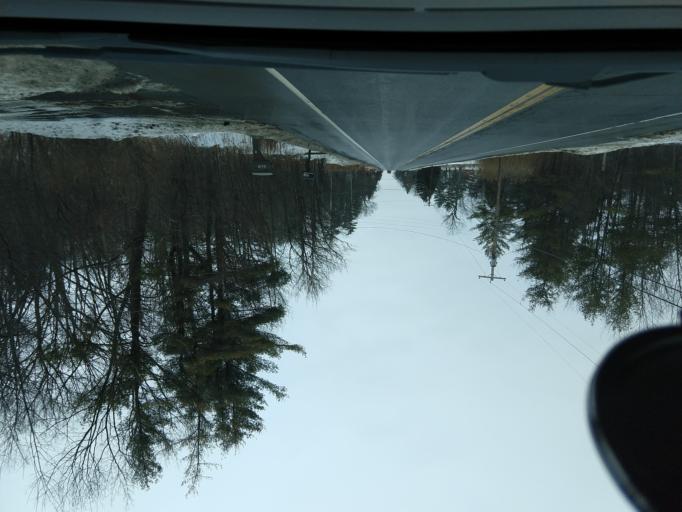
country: US
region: New York
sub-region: Tompkins County
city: Lansing
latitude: 42.5285
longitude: -76.4919
